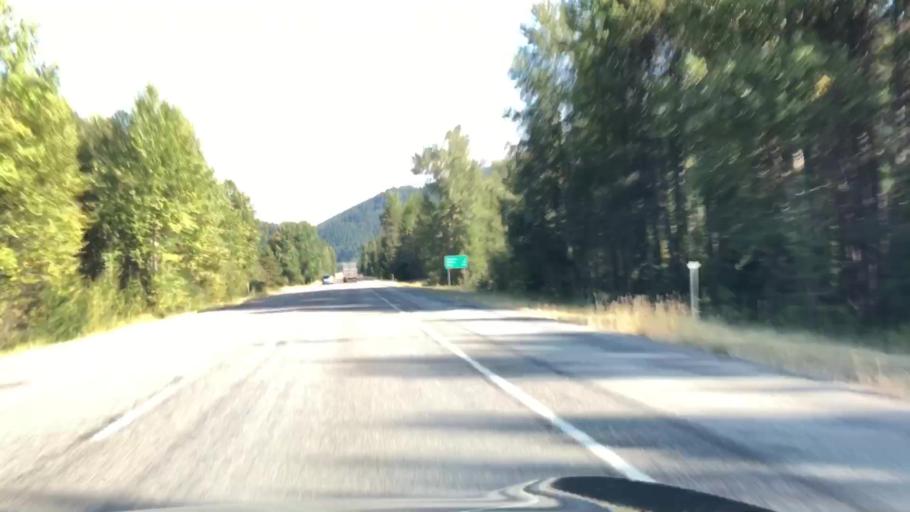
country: US
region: Montana
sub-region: Sanders County
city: Thompson Falls
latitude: 47.3692
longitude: -115.3366
